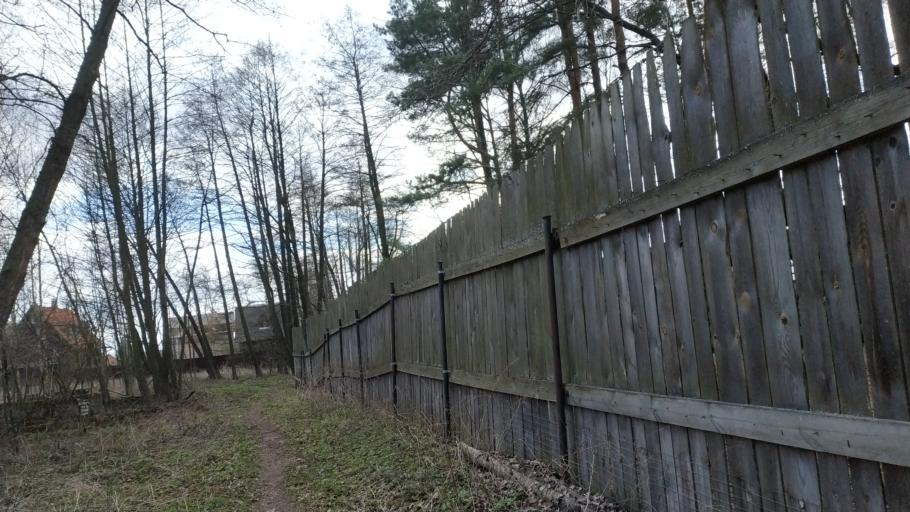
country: RU
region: Moskovskaya
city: Malyshevo
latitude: 55.5438
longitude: 38.3288
